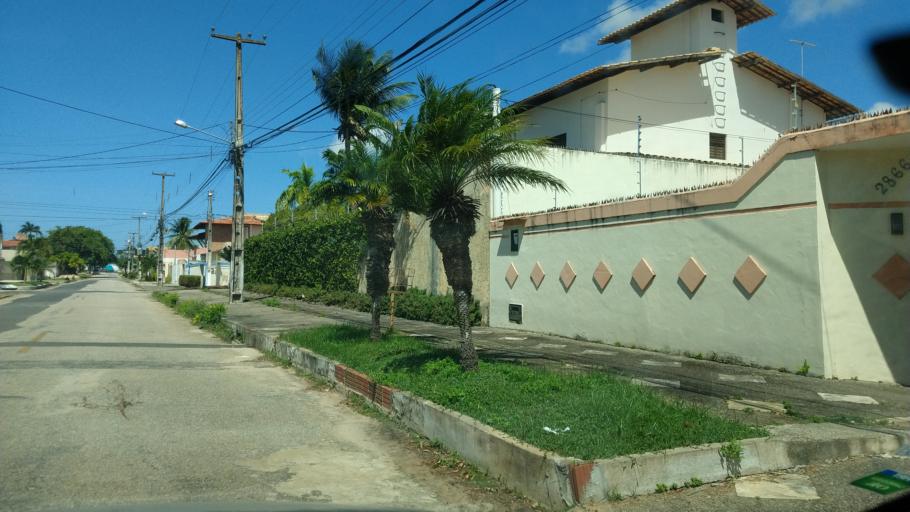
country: BR
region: Rio Grande do Norte
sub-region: Natal
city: Natal
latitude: -5.8456
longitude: -35.2019
